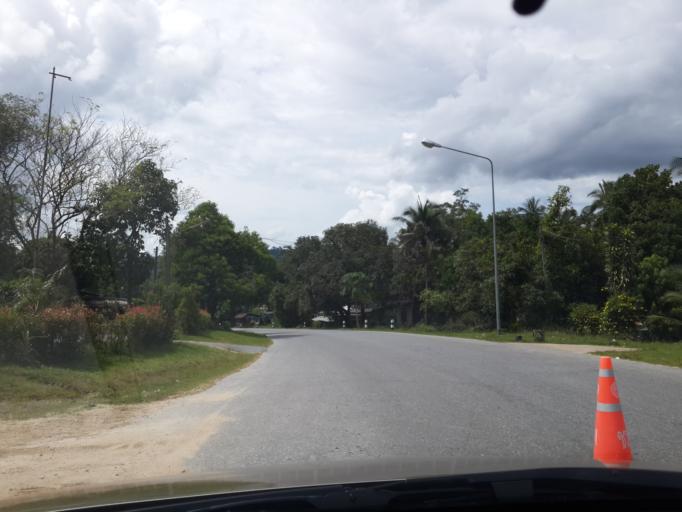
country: TH
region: Yala
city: Raman
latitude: 6.3823
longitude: 101.4103
